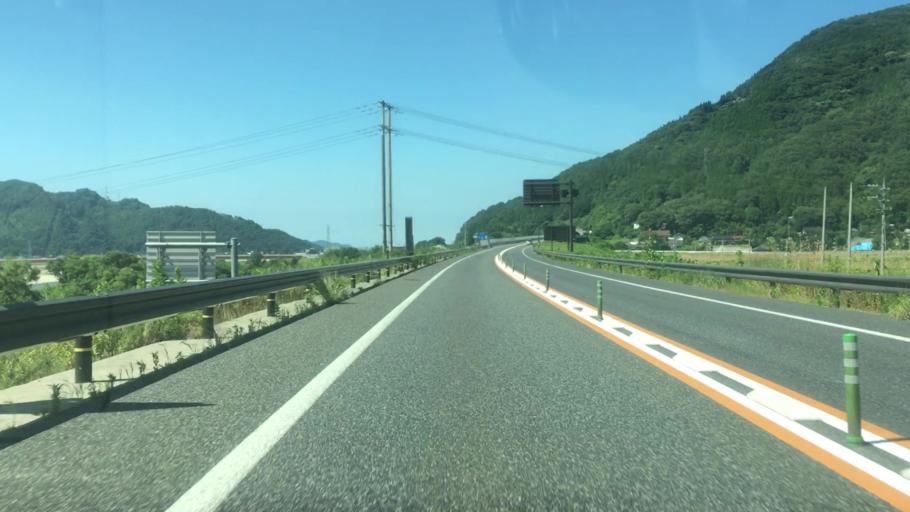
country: JP
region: Tottori
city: Tottori
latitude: 35.4021
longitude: 134.2051
